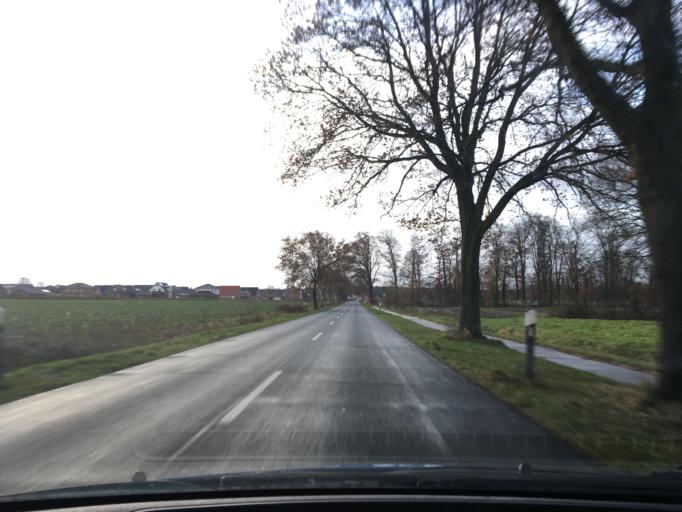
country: DE
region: Lower Saxony
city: Embsen
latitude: 53.1846
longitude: 10.3470
